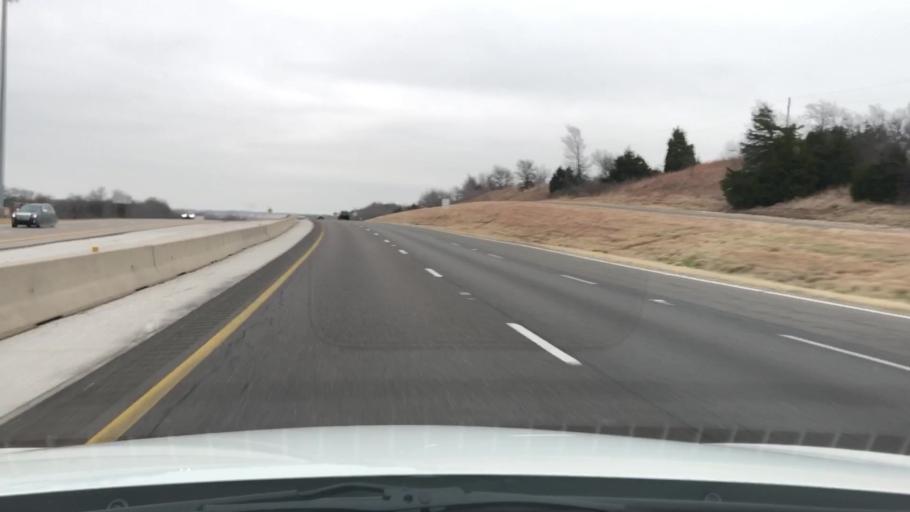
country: US
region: Texas
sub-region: Cooke County
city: Gainesville
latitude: 33.7180
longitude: -97.1610
